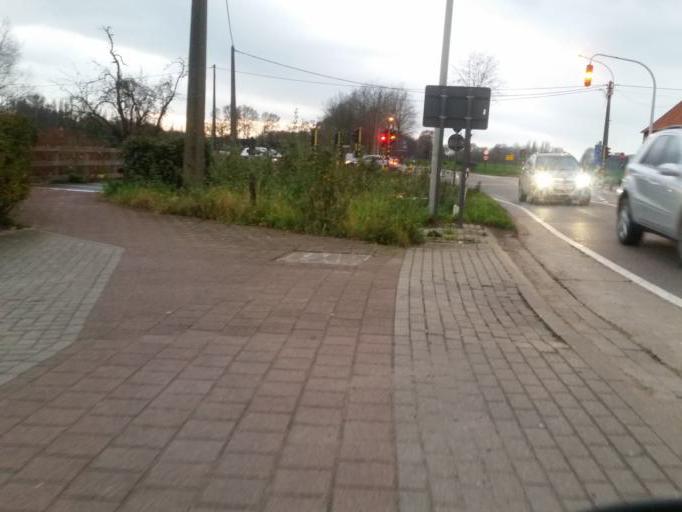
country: BE
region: Flanders
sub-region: Provincie Antwerpen
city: Nijlen
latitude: 51.1794
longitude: 4.6319
